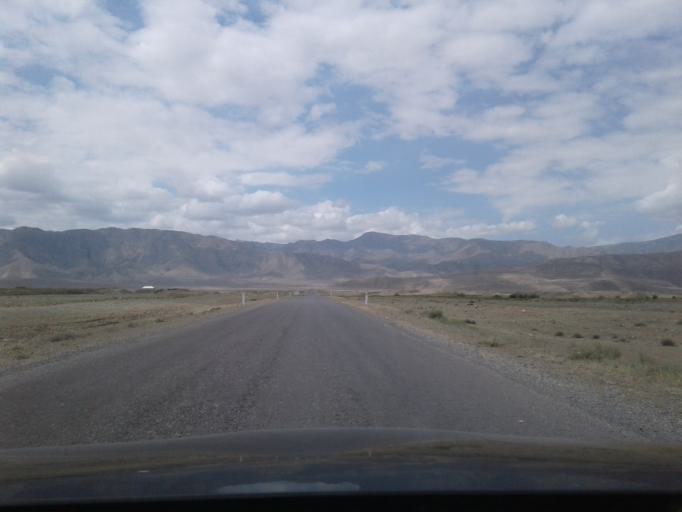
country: TM
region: Ahal
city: Baharly
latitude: 38.5331
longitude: 57.1513
